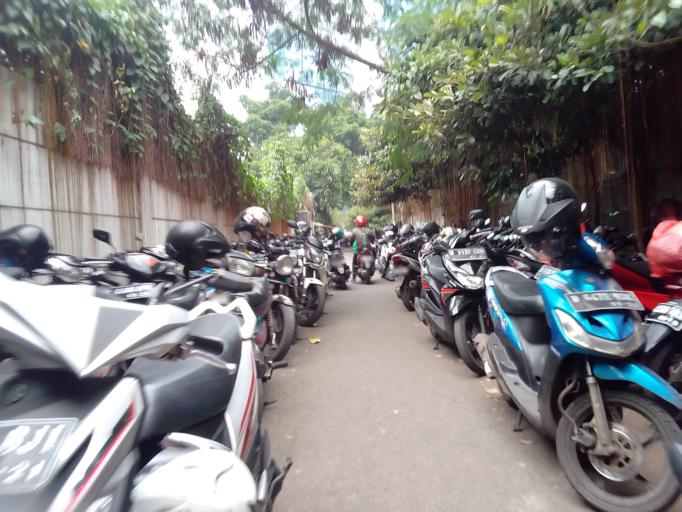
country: ID
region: Jakarta Raya
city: Jakarta
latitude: -6.1969
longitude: 106.8211
